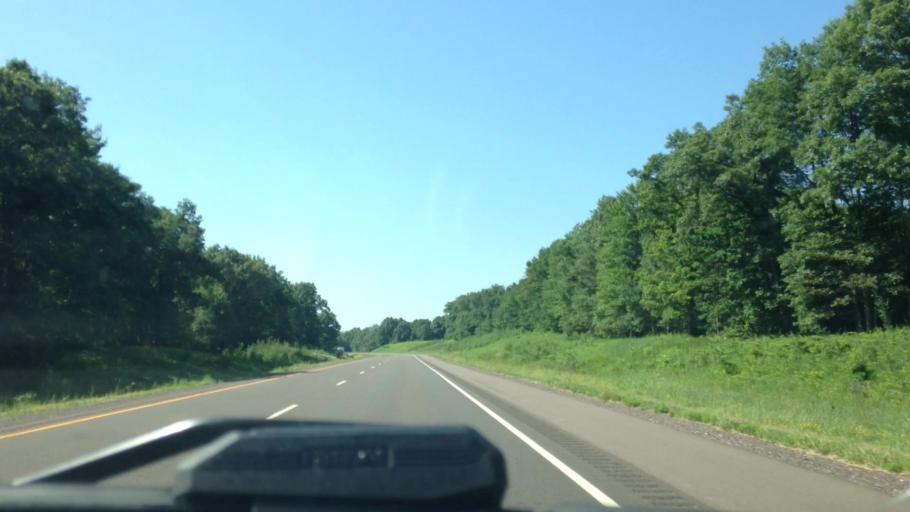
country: US
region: Wisconsin
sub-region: Washburn County
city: Spooner
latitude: 45.9488
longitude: -91.8287
